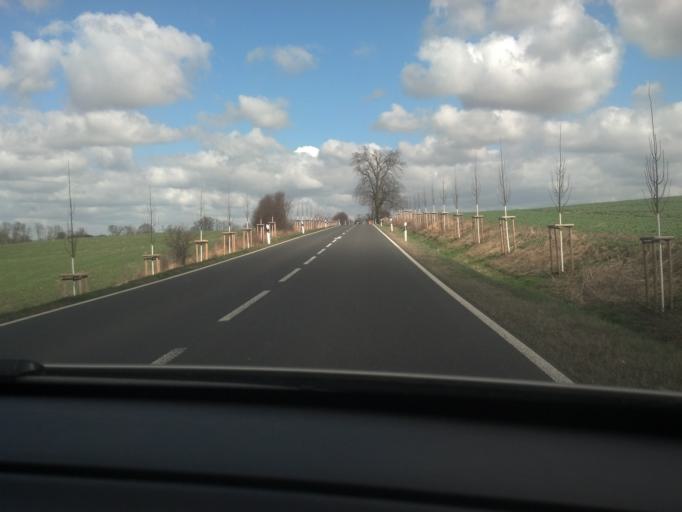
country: DE
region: Mecklenburg-Vorpommern
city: Blankensee
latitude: 53.3815
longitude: 13.3275
